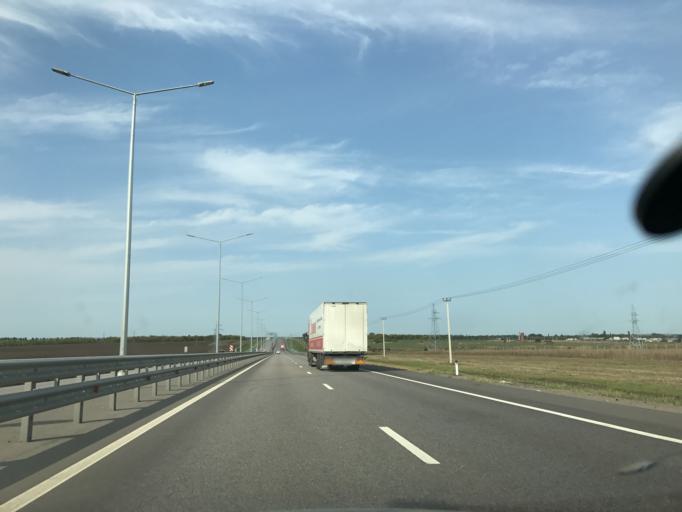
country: RU
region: Voronezj
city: Kashirskoye
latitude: 51.4891
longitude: 39.5323
